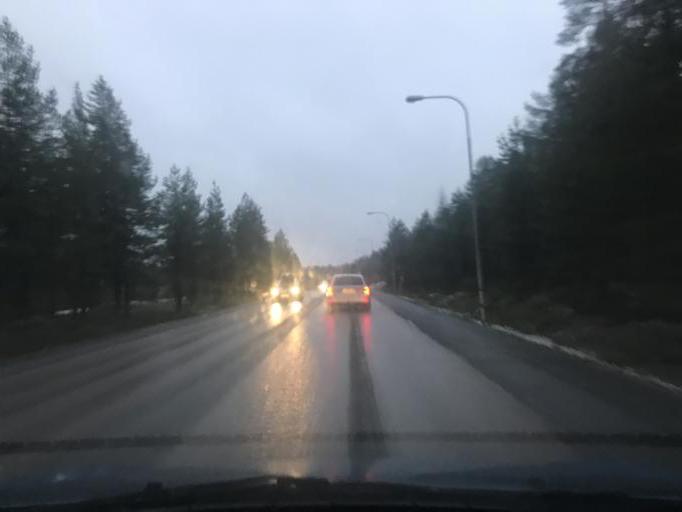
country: SE
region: Norrbotten
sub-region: Lulea Kommun
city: Gammelstad
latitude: 65.6241
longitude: 22.0358
